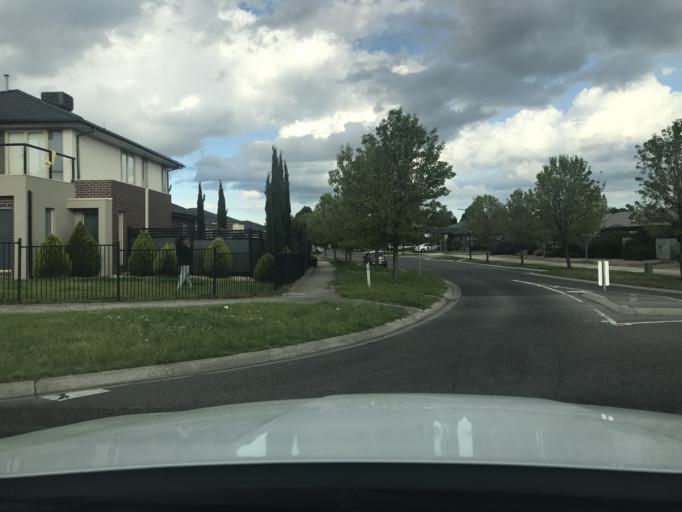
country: AU
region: Victoria
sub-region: Hume
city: Craigieburn
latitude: -37.5825
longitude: 144.9074
